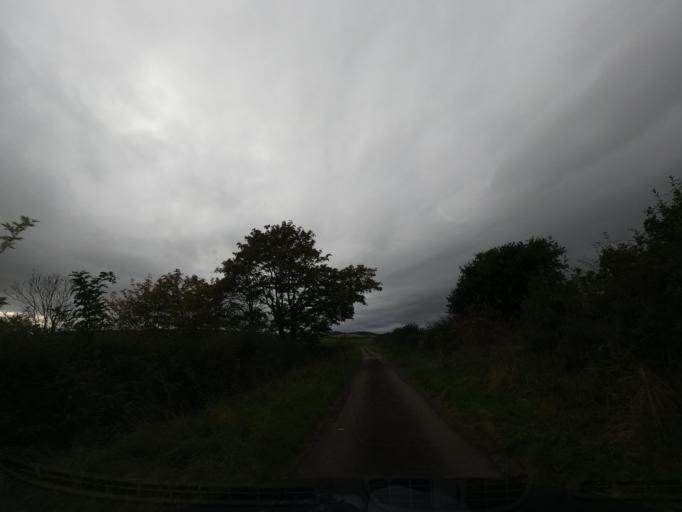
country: GB
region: England
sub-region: Northumberland
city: Ford
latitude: 55.6079
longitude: -2.0531
